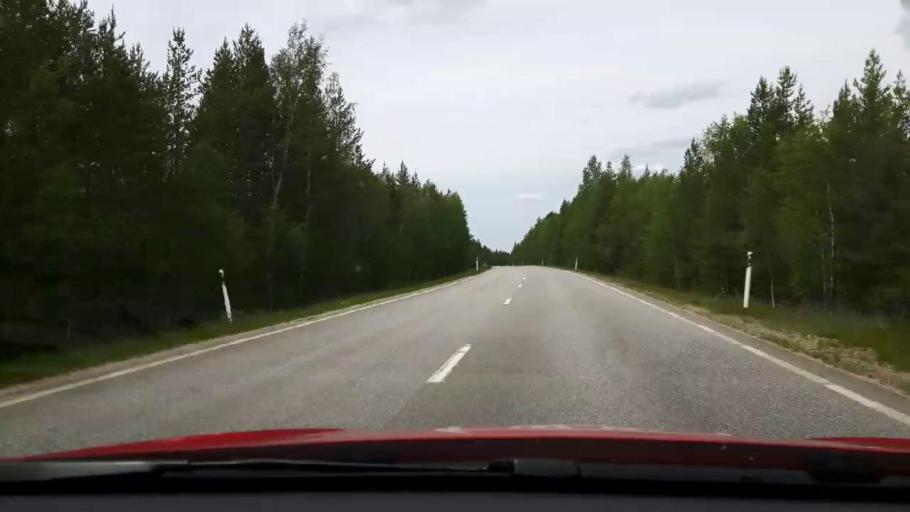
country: SE
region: Jaemtland
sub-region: Harjedalens Kommun
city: Sveg
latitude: 62.0775
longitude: 14.2648
